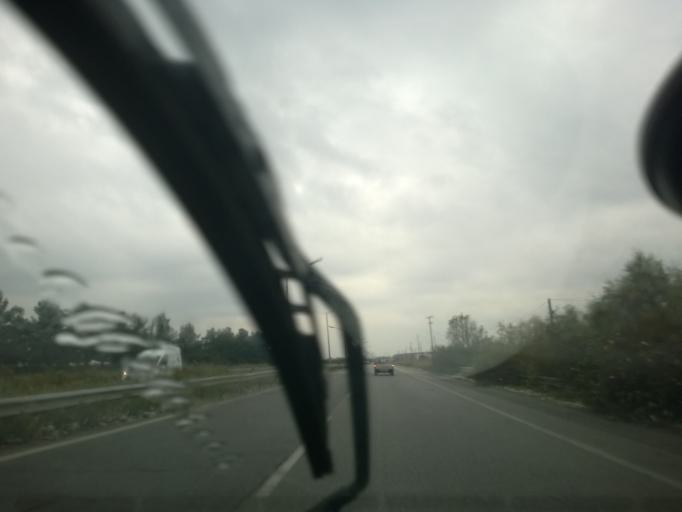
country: GR
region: Central Macedonia
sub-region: Nomos Thessalonikis
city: Agios Athanasios
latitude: 40.7122
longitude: 22.7545
